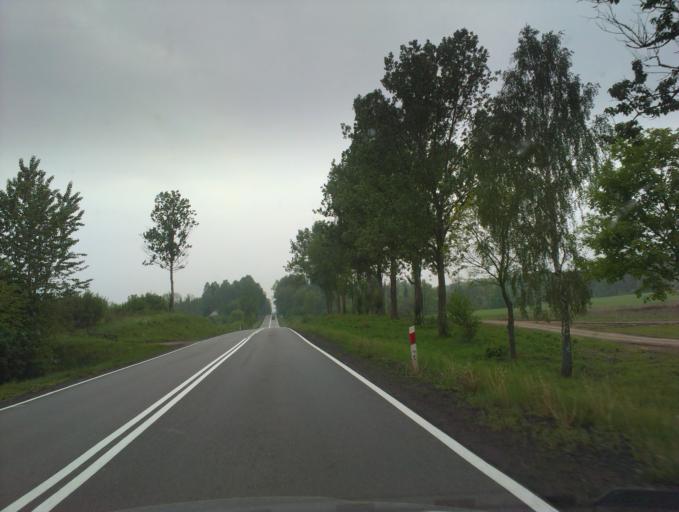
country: PL
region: West Pomeranian Voivodeship
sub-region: Powiat koszalinski
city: Bobolice
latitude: 53.9057
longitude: 16.6110
